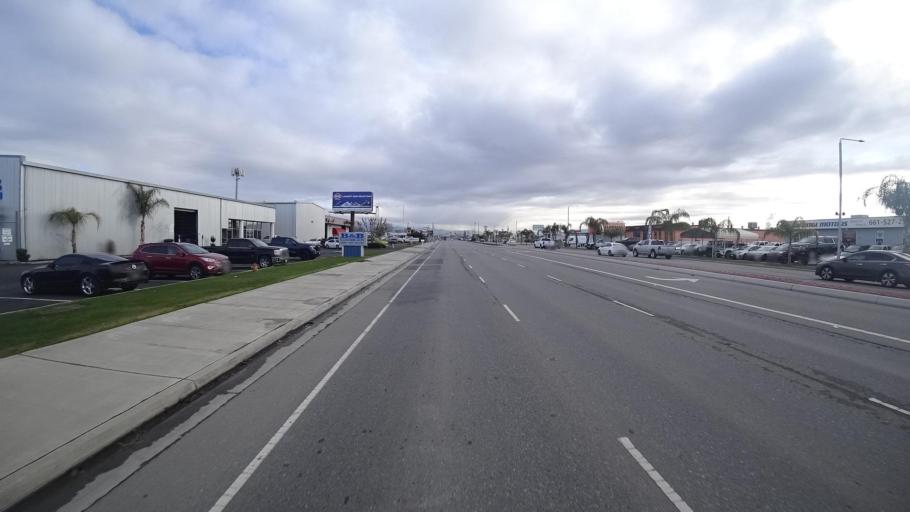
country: US
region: California
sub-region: Kern County
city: Greenacres
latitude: 35.3834
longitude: -119.0782
